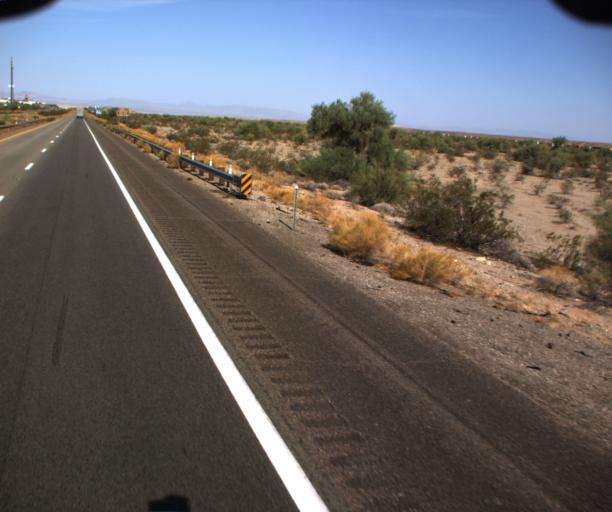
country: US
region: Arizona
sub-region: Mohave County
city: Desert Hills
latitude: 34.7303
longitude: -114.2994
